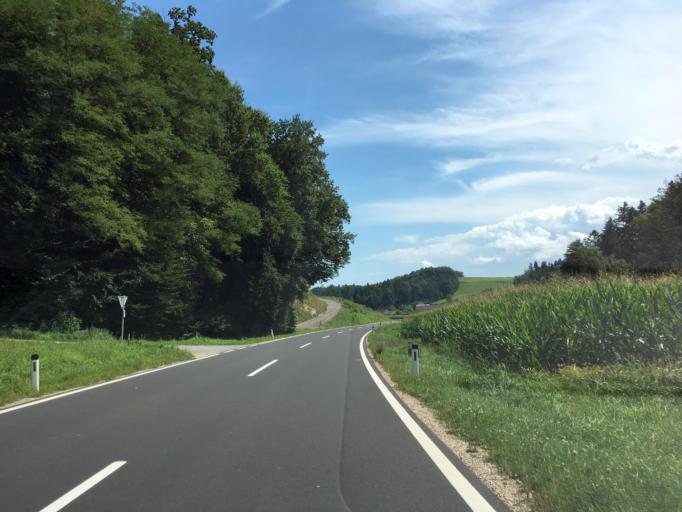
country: AT
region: Styria
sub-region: Politischer Bezirk Leibnitz
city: Gleinstatten
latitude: 46.7379
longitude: 15.3752
